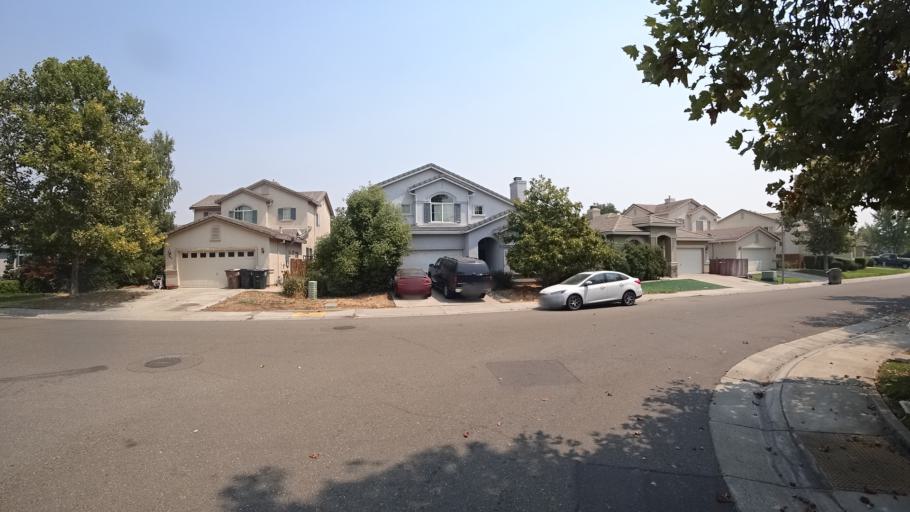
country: US
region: California
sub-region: Sacramento County
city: Laguna
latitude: 38.4069
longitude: -121.4346
